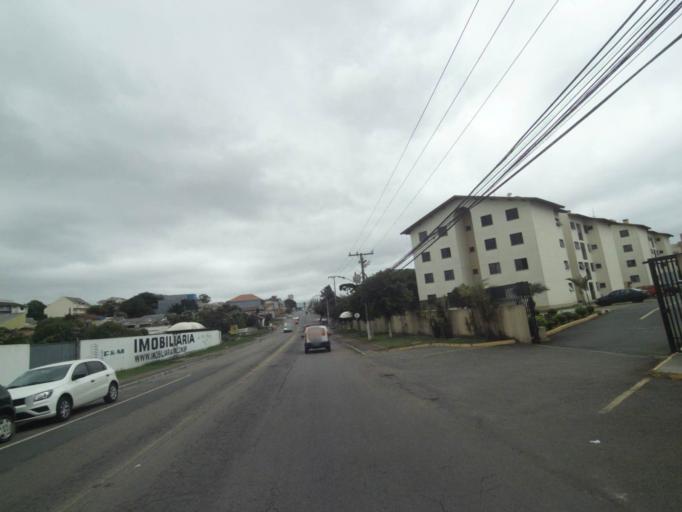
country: BR
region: Parana
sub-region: Curitiba
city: Curitiba
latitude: -25.4926
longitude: -49.3045
